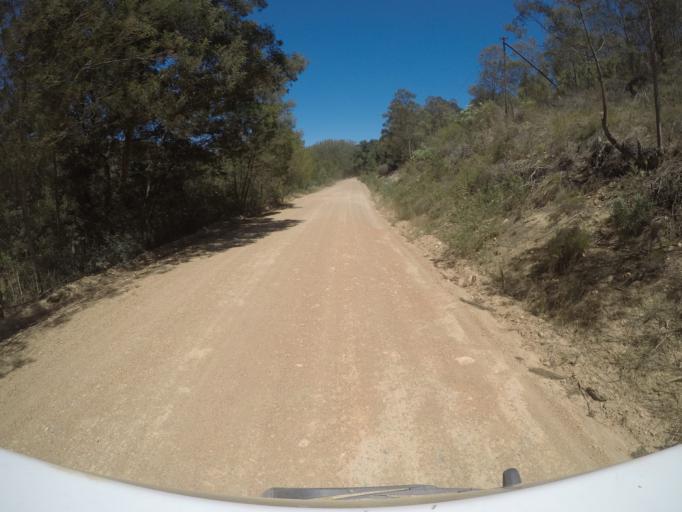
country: ZA
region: Western Cape
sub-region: Overberg District Municipality
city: Caledon
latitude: -34.1556
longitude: 19.2312
